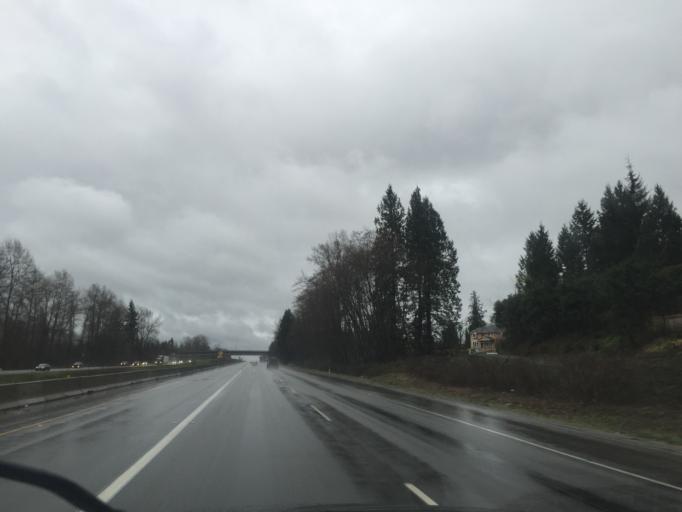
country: CA
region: British Columbia
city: Walnut Grove
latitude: 49.1597
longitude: -122.6527
